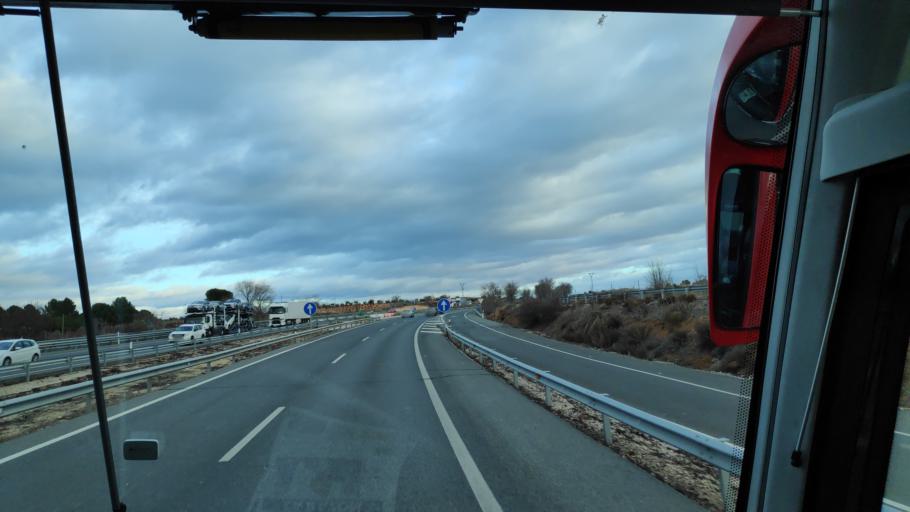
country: ES
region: Madrid
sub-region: Provincia de Madrid
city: Villarejo de Salvanes
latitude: 40.1624
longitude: -3.2662
